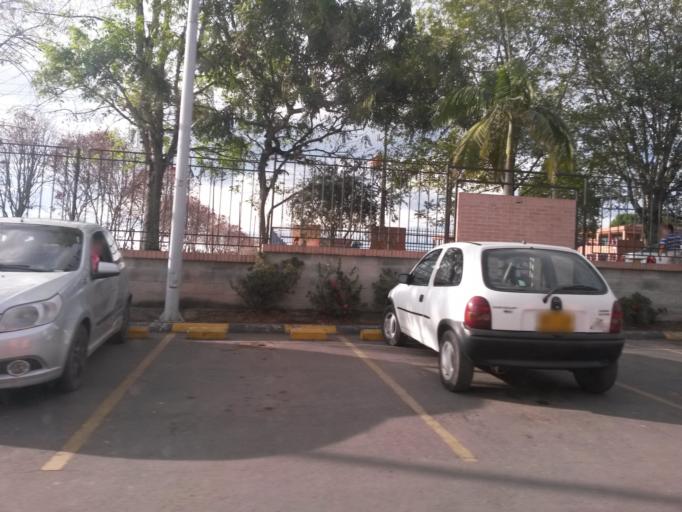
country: CO
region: Cauca
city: Popayan
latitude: 2.4603
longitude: -76.5947
